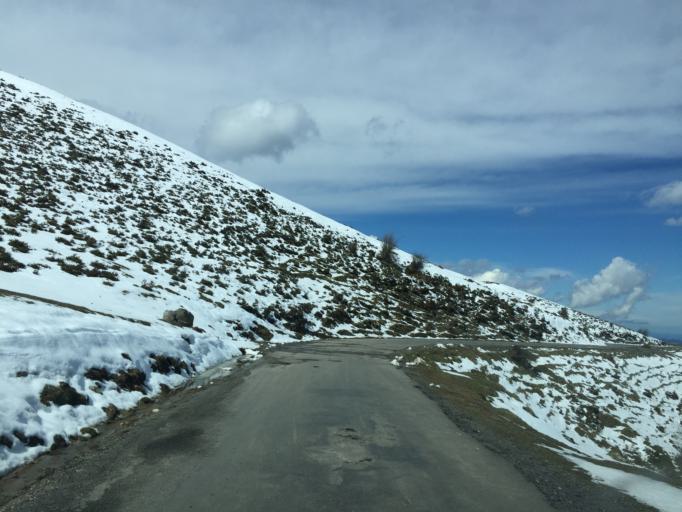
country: ES
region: Asturias
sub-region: Province of Asturias
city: Amieva
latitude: 43.2740
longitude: -4.9820
